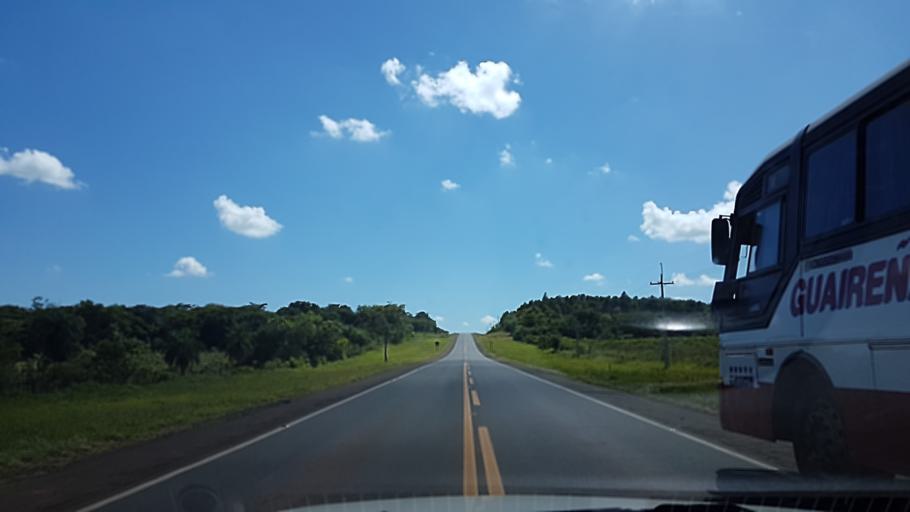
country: PY
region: Itapua
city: Carmen del Parana
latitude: -27.2190
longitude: -56.0982
